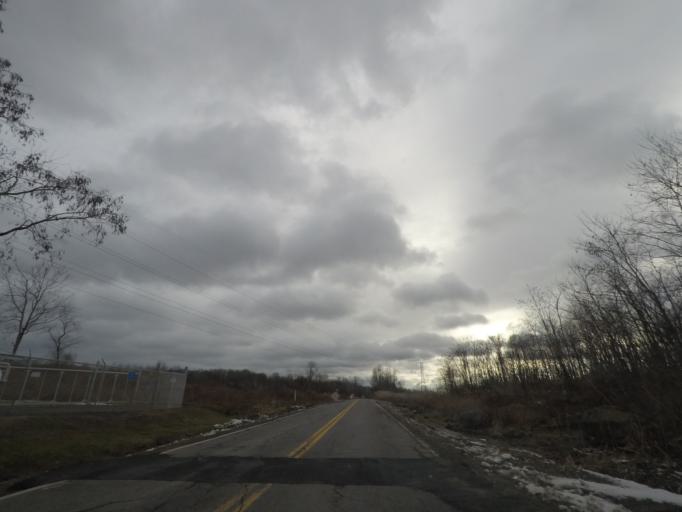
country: US
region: New York
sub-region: Rensselaer County
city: East Greenbush
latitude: 42.5940
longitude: -73.7202
